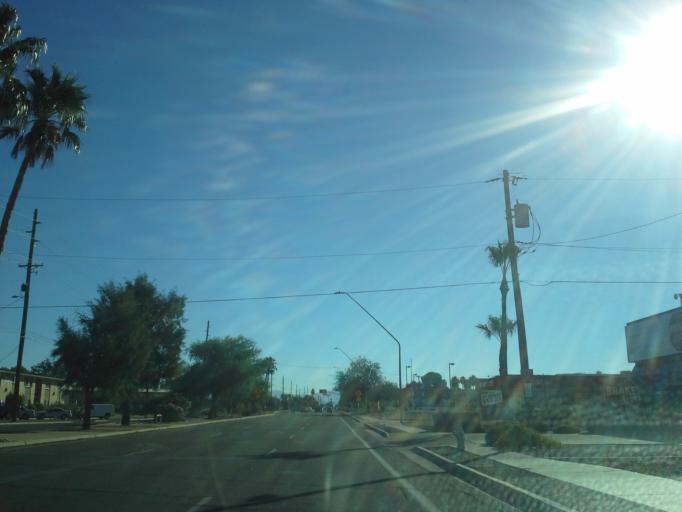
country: US
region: Arizona
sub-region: Pima County
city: Drexel Heights
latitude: 32.1339
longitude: -110.9754
